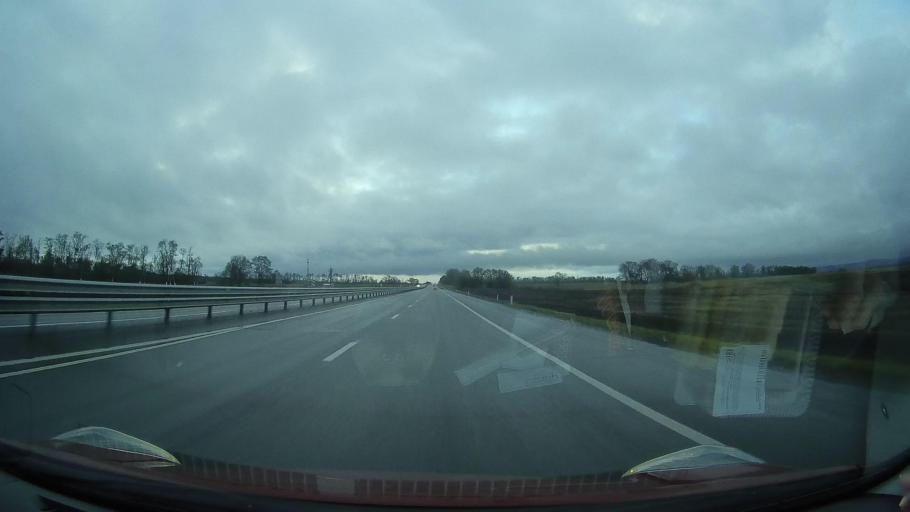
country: RU
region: Stavropol'skiy
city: Zavetnoye
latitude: 44.7849
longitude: 41.5194
